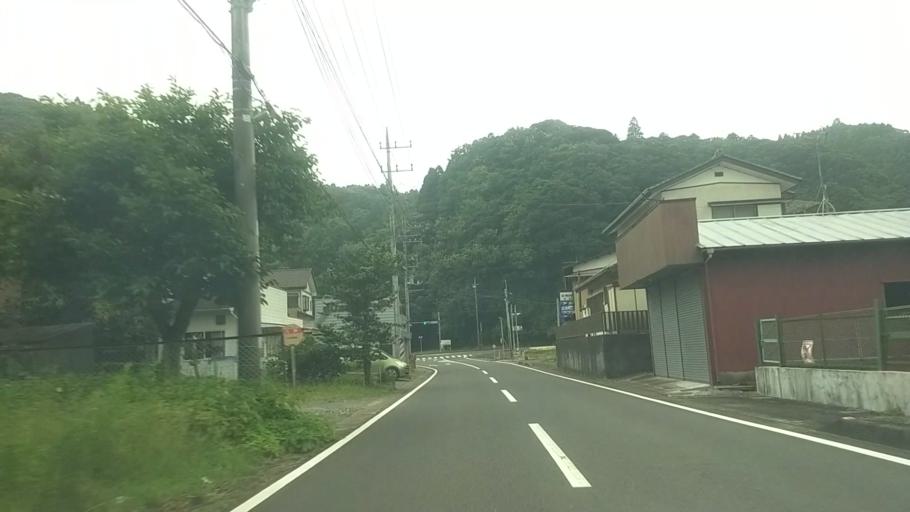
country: JP
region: Chiba
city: Ohara
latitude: 35.2700
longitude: 140.2547
